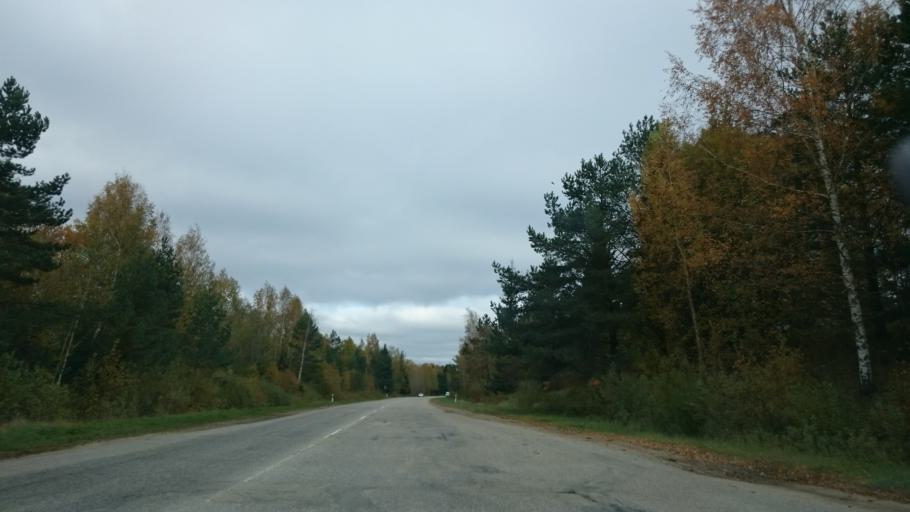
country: LV
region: Amatas Novads
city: Drabesi
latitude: 57.2355
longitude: 25.2536
